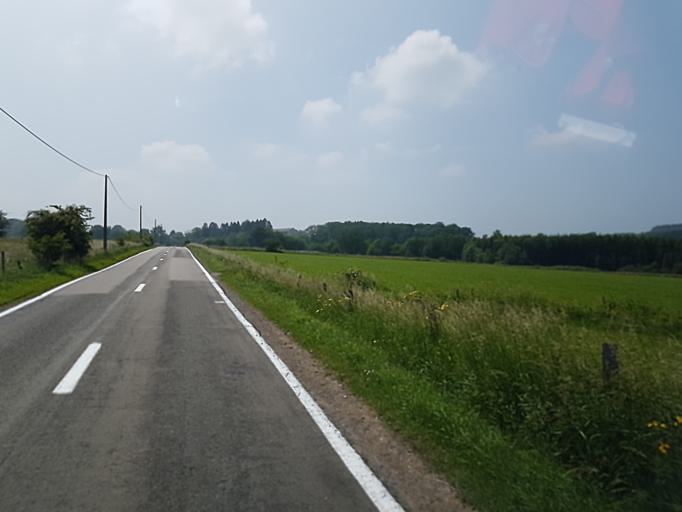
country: BE
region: Wallonia
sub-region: Province du Luxembourg
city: Manhay
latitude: 50.2968
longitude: 5.6871
